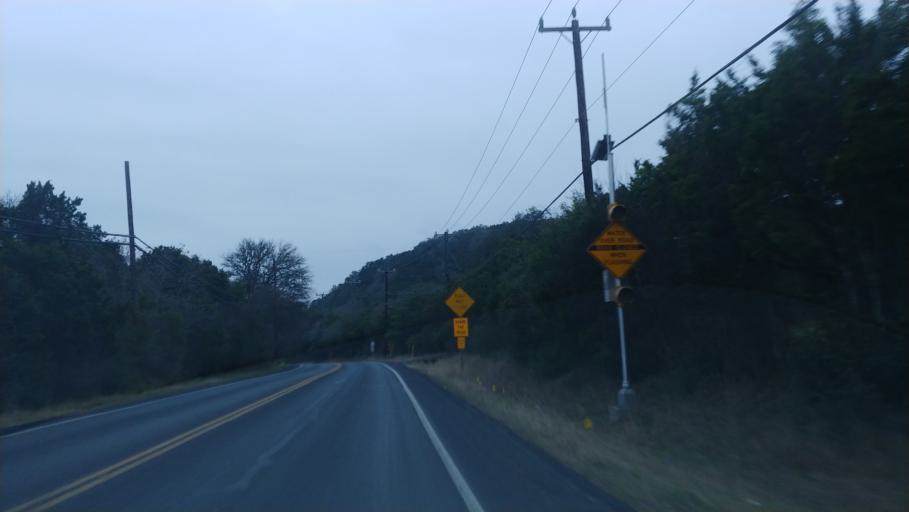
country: US
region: Texas
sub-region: Bexar County
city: Helotes
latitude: 29.5907
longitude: -98.6892
